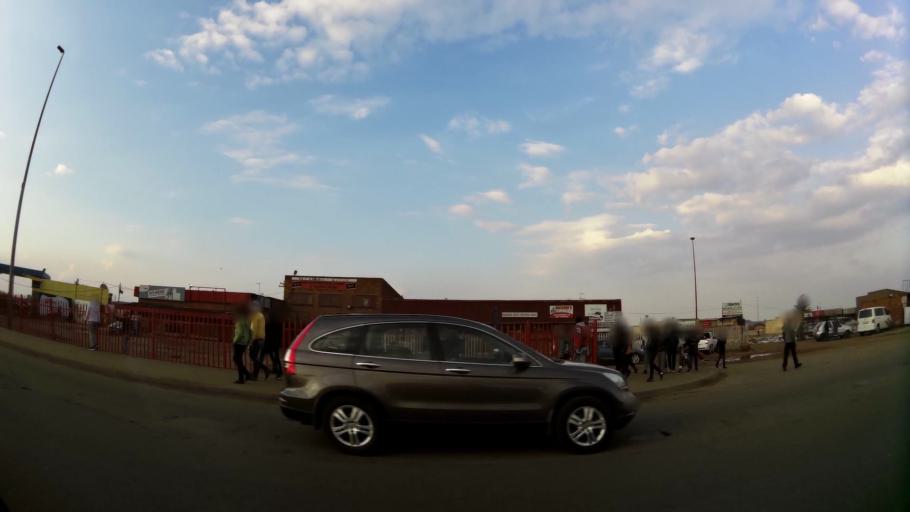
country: ZA
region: Gauteng
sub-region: City of Johannesburg Metropolitan Municipality
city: Orange Farm
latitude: -26.5812
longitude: 27.8428
